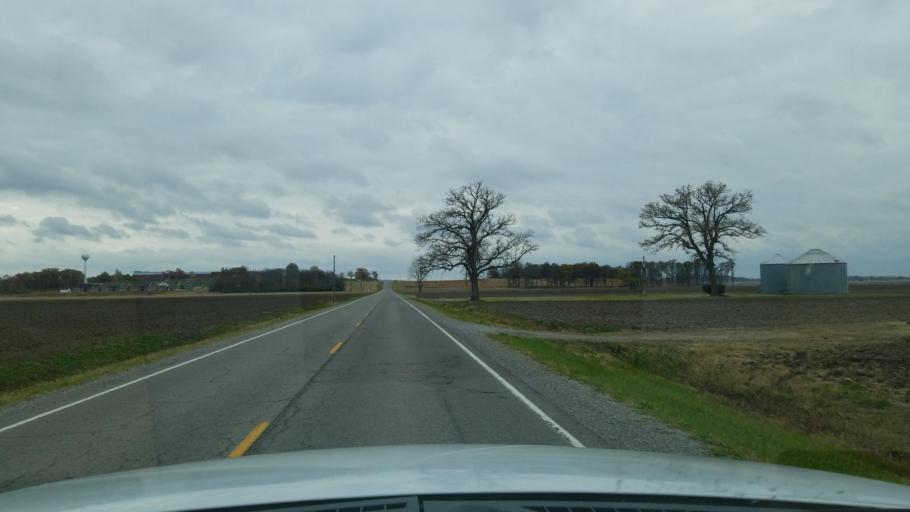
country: US
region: Illinois
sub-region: Saline County
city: Eldorado
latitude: 37.7615
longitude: -88.4383
